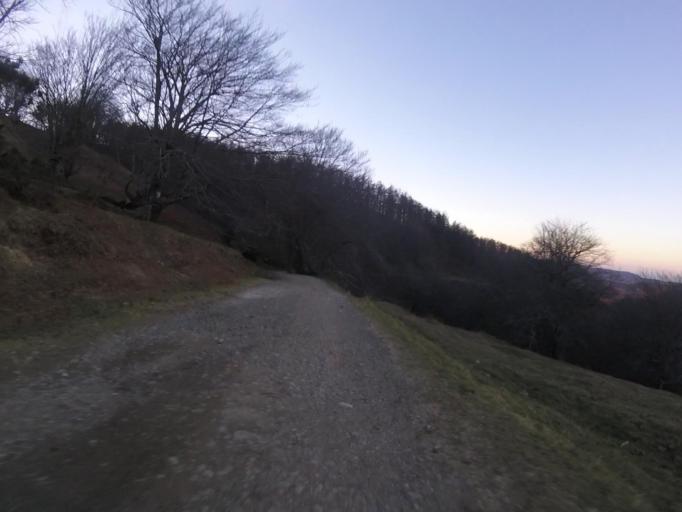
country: ES
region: Navarre
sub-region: Provincia de Navarra
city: Arano
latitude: 43.2557
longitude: -1.8254
